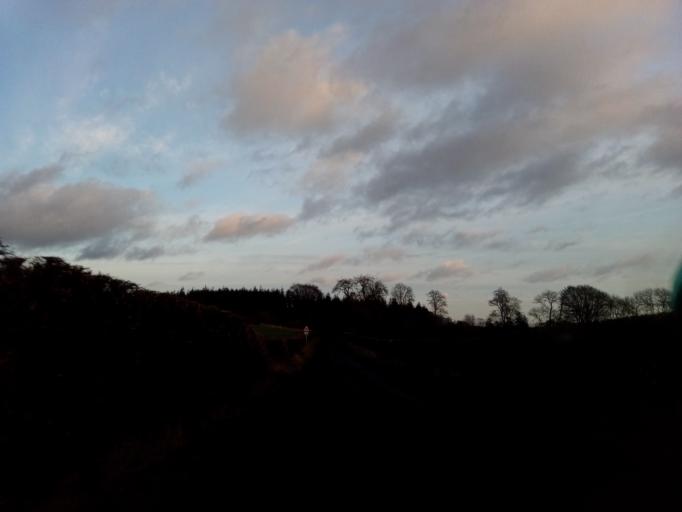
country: GB
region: Scotland
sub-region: The Scottish Borders
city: Newtown St Boswells
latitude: 55.5496
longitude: -2.6967
